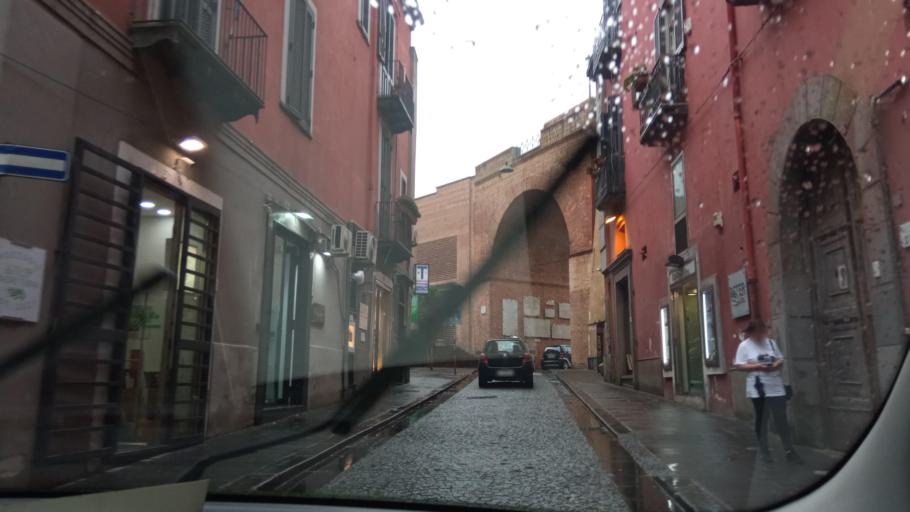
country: IT
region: Campania
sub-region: Provincia di Napoli
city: Pozzuoli
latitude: 40.8220
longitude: 14.1218
